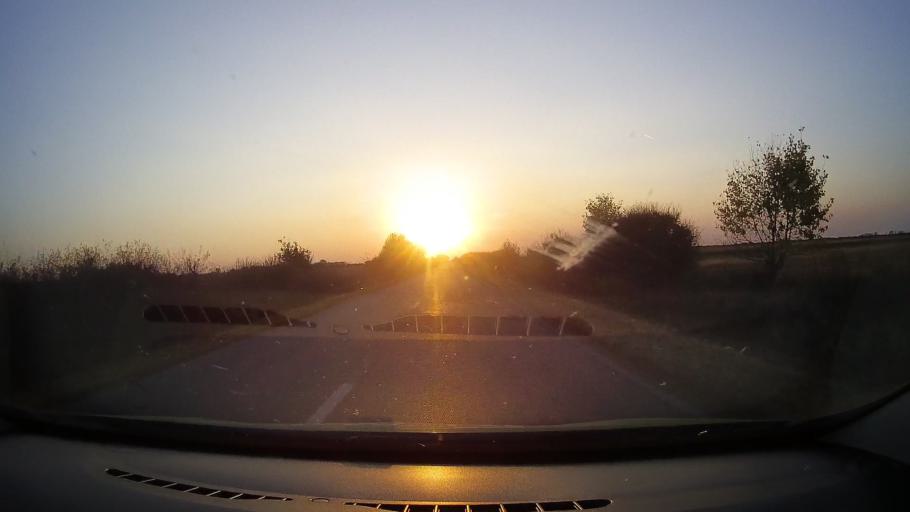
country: RO
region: Arad
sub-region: Comuna Seleus
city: Seleus
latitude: 46.3823
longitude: 21.6818
